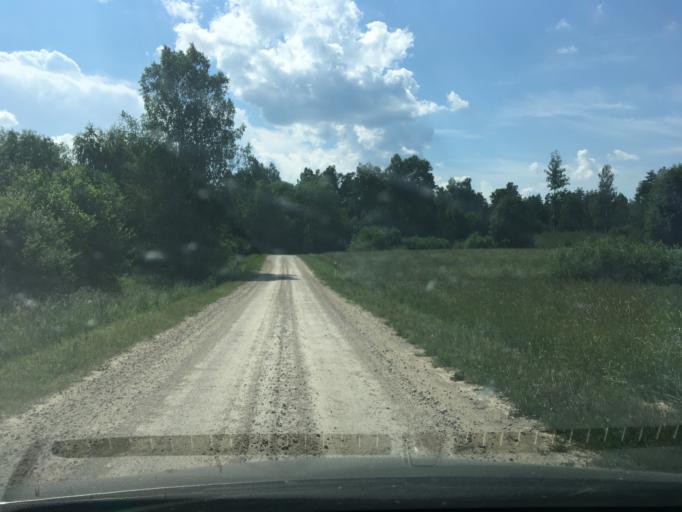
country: EE
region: Raplamaa
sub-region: Maerjamaa vald
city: Marjamaa
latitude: 58.8069
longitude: 24.4332
